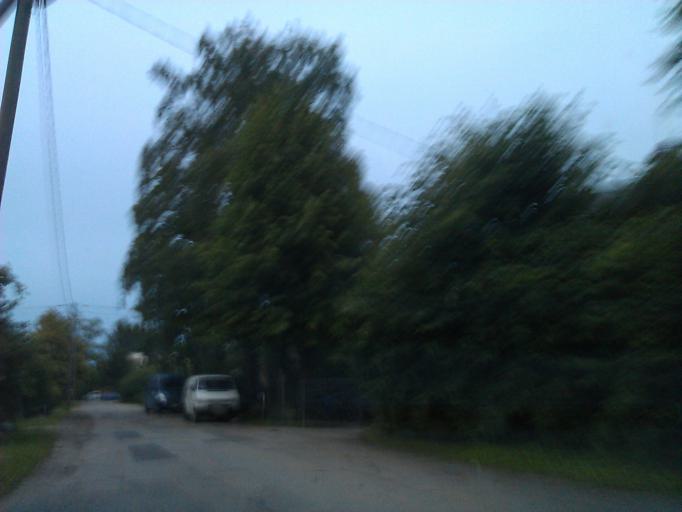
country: LV
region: Sigulda
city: Sigulda
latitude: 57.1467
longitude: 24.8432
